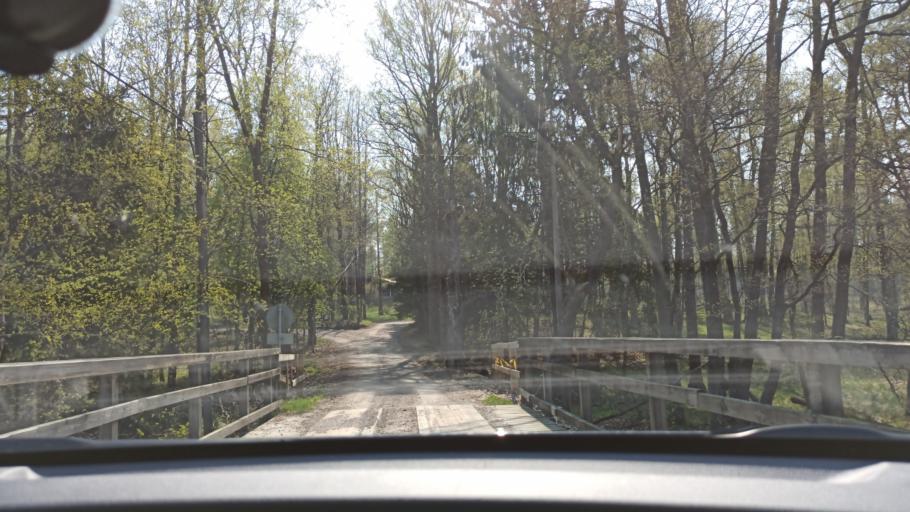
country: FI
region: Uusimaa
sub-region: Helsinki
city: Espoo
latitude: 60.1053
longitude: 24.6342
